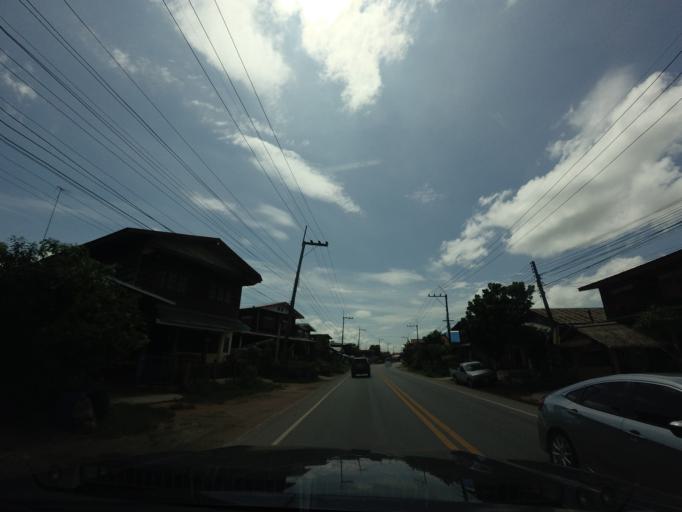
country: TH
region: Changwat Udon Thani
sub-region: Amphoe Ban Phue
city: Ban Phue
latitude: 17.7496
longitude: 102.3991
